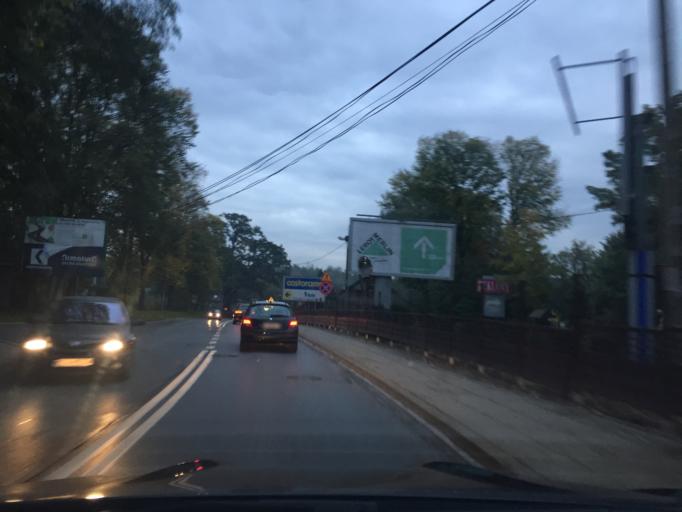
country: PL
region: Lesser Poland Voivodeship
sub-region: Powiat krakowski
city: Wrzasowice
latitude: 50.0075
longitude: 19.9325
